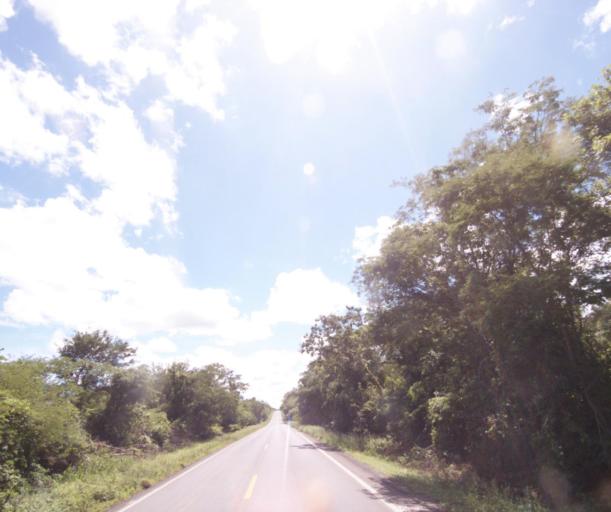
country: BR
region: Bahia
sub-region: Sao Felix Do Coribe
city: Santa Maria da Vitoria
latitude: -13.3926
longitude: -44.1205
